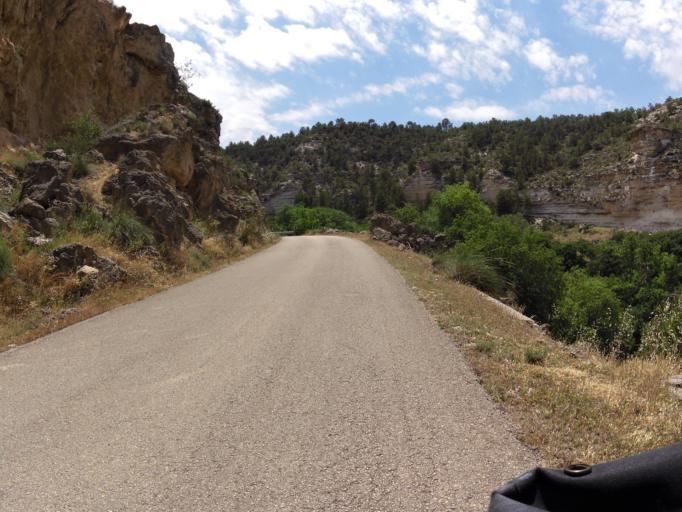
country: ES
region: Castille-La Mancha
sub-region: Provincia de Albacete
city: Casas de Juan Nunez
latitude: 39.1600
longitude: -1.6029
